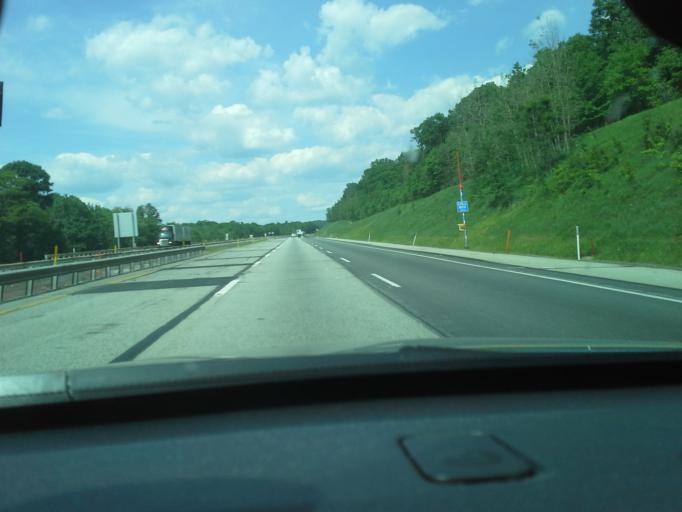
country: US
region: Pennsylvania
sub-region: Bedford County
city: Earlston
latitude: 39.9901
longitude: -78.2289
